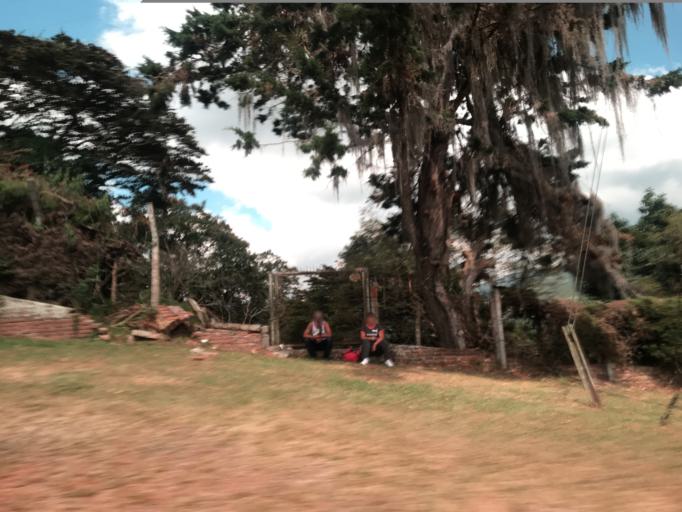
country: CO
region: Valle del Cauca
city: Cali
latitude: 3.4830
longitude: -76.6086
